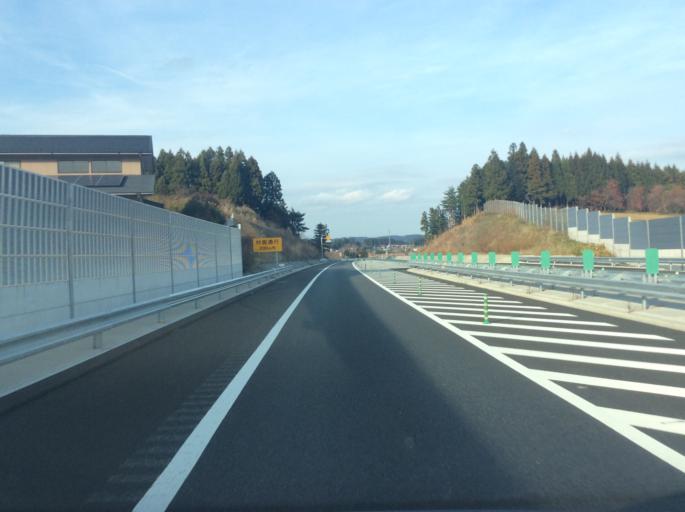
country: JP
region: Fukushima
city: Namie
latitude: 37.5362
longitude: 140.9407
